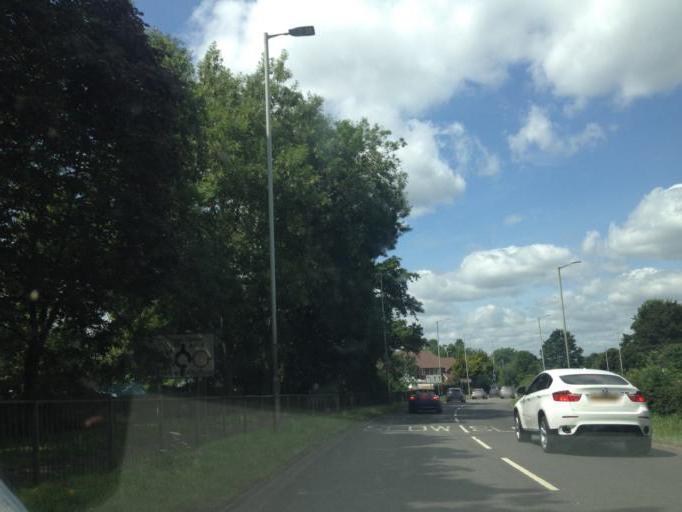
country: GB
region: England
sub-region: Hertfordshire
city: Hemel Hempstead
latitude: 51.7490
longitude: -0.4482
